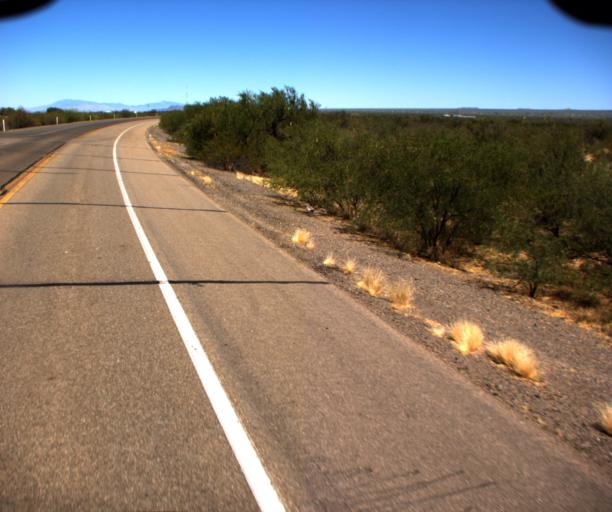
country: US
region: Arizona
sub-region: Pima County
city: Three Points
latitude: 32.0759
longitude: -111.3445
